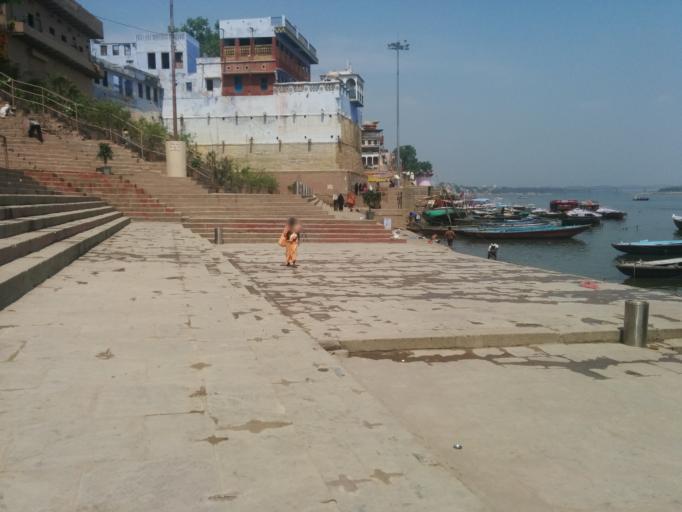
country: IN
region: Uttar Pradesh
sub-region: Varanasi
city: Varanasi
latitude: 25.3077
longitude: 83.0111
